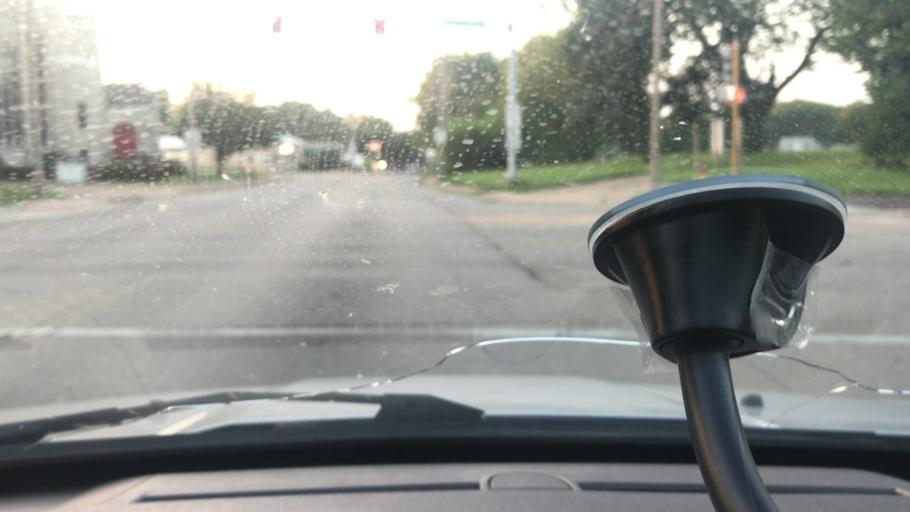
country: US
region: Illinois
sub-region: Tazewell County
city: Pekin
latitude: 40.5676
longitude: -89.6408
